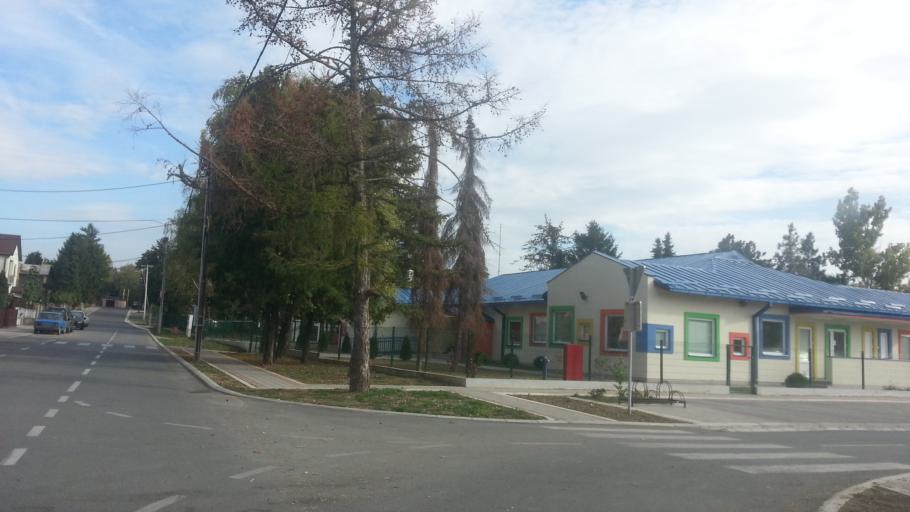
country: RS
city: Belegis
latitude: 45.0178
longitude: 20.3346
